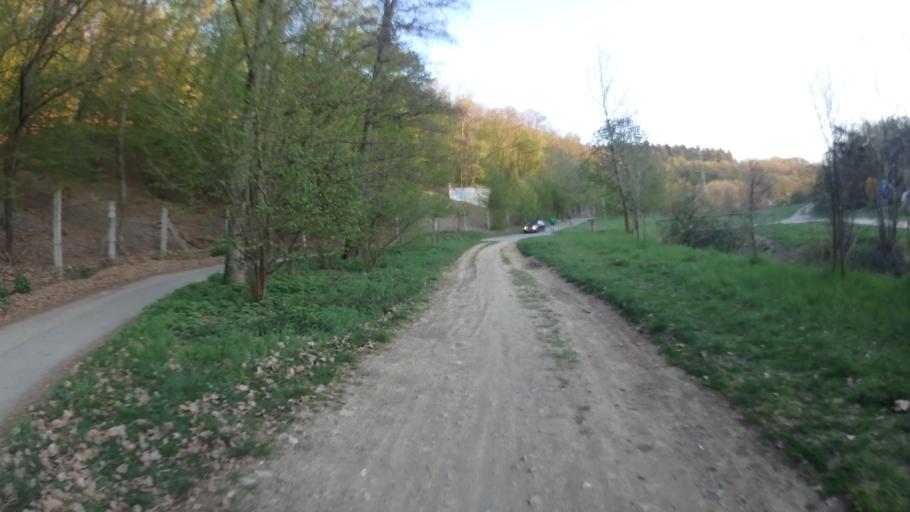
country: CZ
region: South Moravian
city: Troubsko
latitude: 49.2140
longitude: 16.5271
